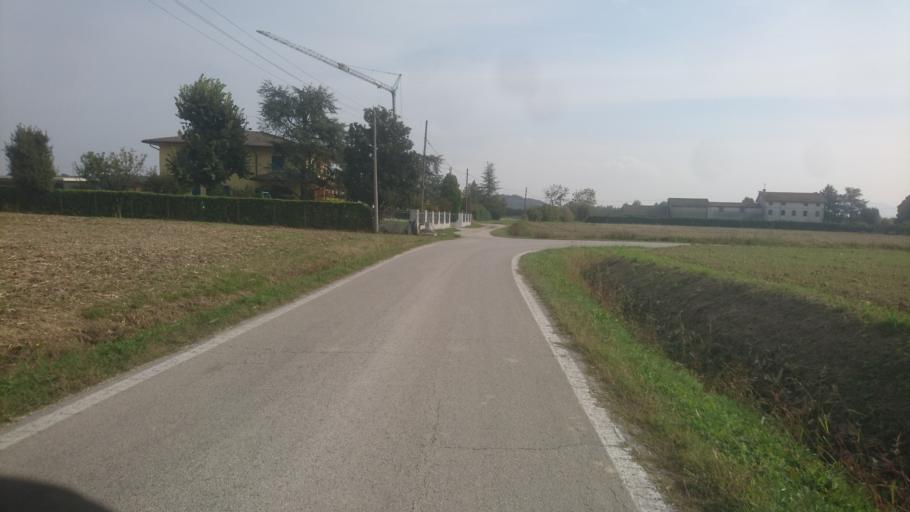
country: IT
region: Veneto
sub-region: Provincia di Vicenza
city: Montegalda
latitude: 45.4644
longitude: 11.6549
